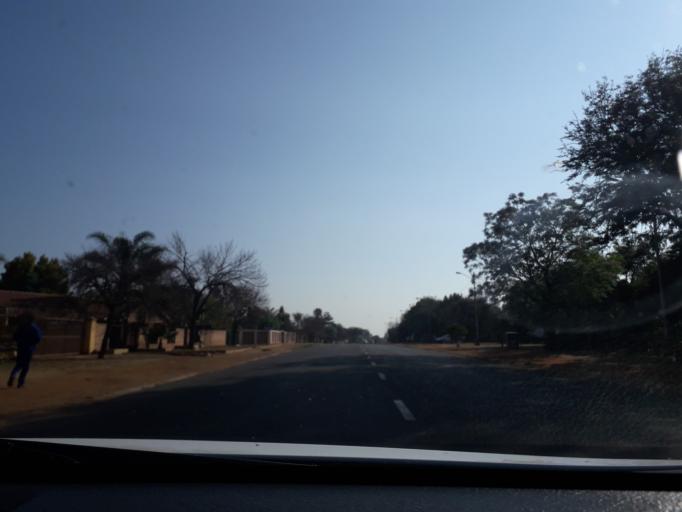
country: ZA
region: Gauteng
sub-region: City of Johannesburg Metropolitan Municipality
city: Modderfontein
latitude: -26.0960
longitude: 28.2414
